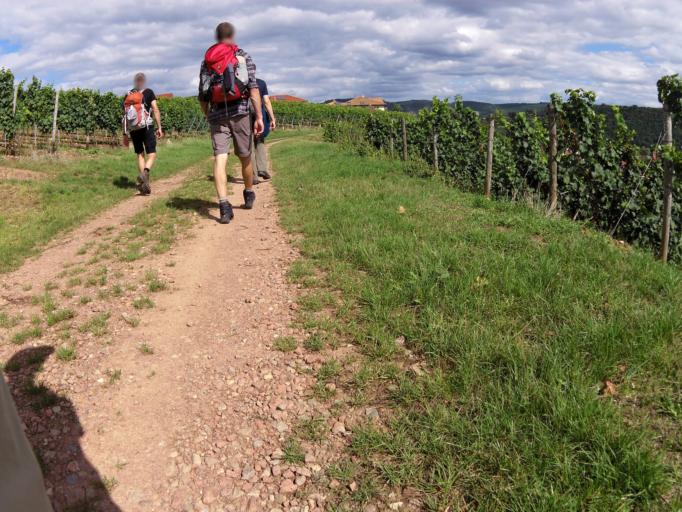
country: DE
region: Rheinland-Pfalz
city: Huffelsheim
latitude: 49.8106
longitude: 7.8055
